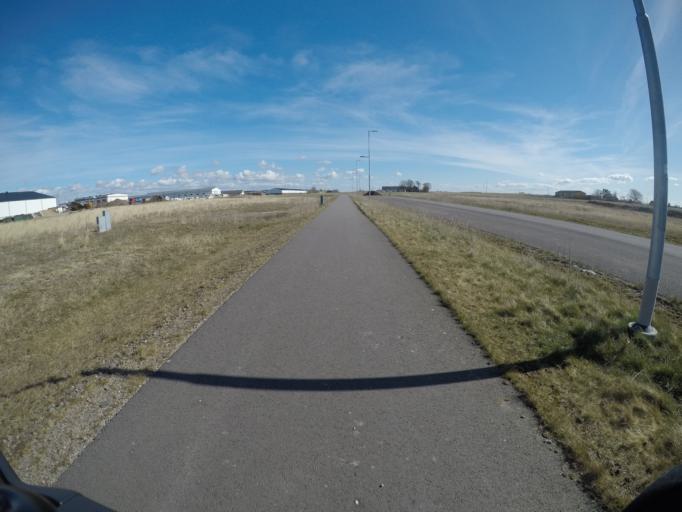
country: SE
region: Halland
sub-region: Laholms Kommun
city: Laholm
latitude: 56.4976
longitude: 13.0119
